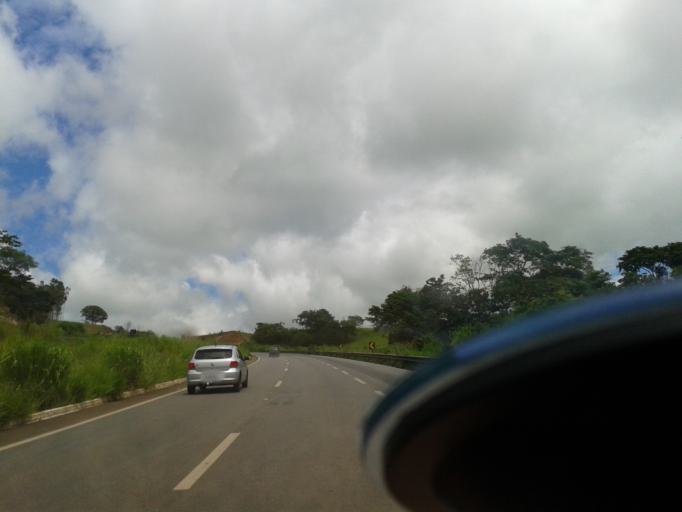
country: BR
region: Goias
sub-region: Itaberai
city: Itaberai
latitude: -16.1609
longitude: -49.6231
